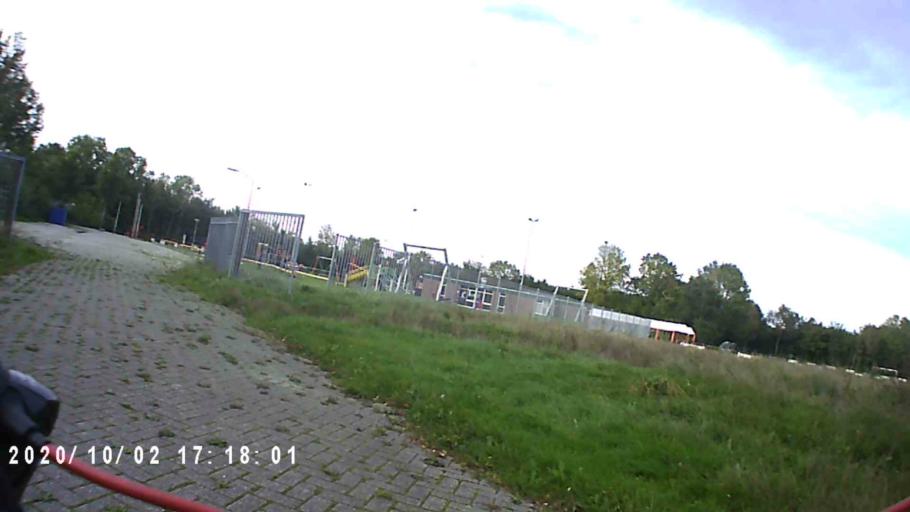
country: NL
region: Groningen
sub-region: Gemeente De Marne
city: Ulrum
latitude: 53.3399
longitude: 6.3072
